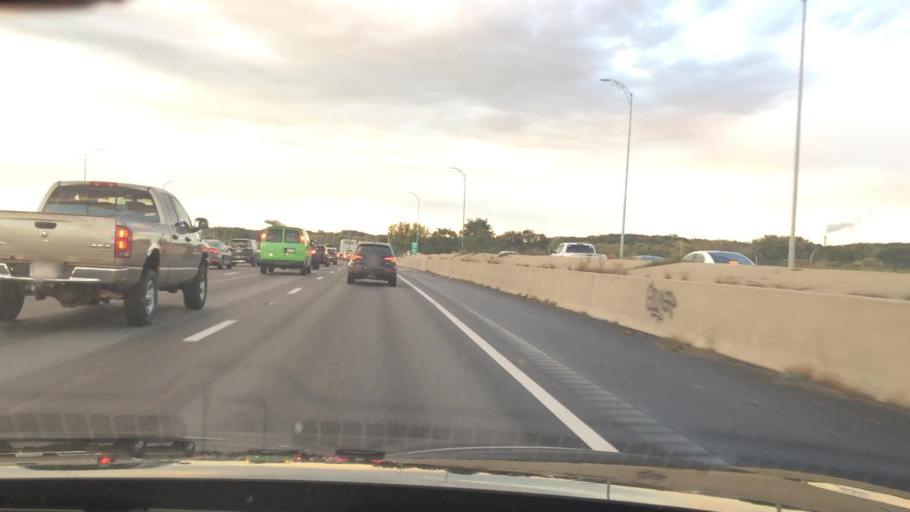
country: US
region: Massachusetts
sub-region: Essex County
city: North Andover
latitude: 42.7104
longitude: -71.1375
